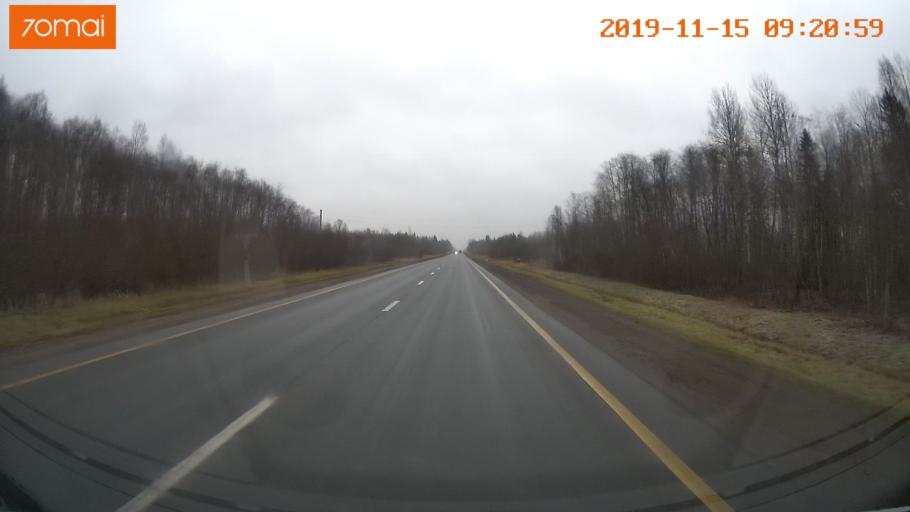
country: RU
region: Vologda
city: Tonshalovo
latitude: 59.2928
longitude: 38.0517
